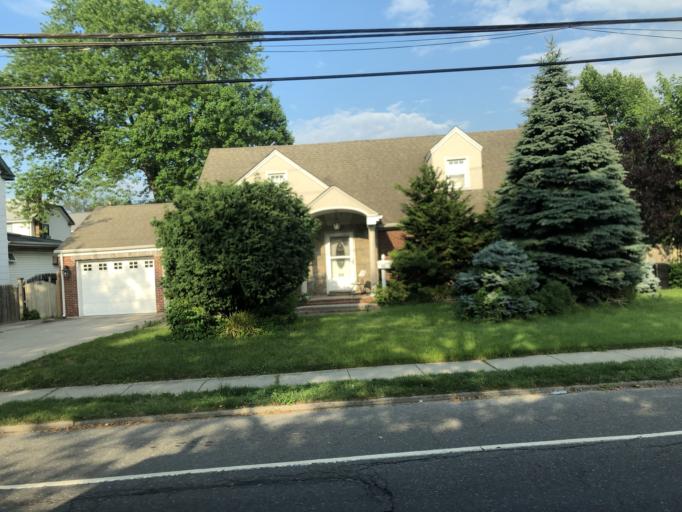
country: US
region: New York
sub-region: Nassau County
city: Malverne
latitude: 40.6695
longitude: -73.6729
